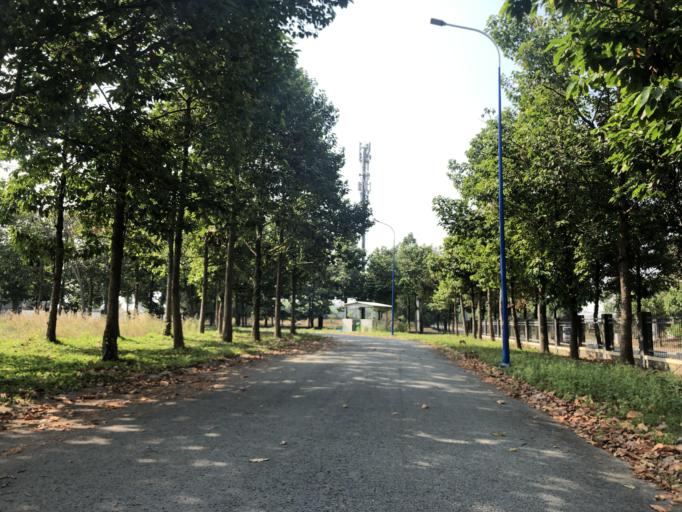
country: VN
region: Binh Duong
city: Thu Dau Mot
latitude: 11.0521
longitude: 106.6636
